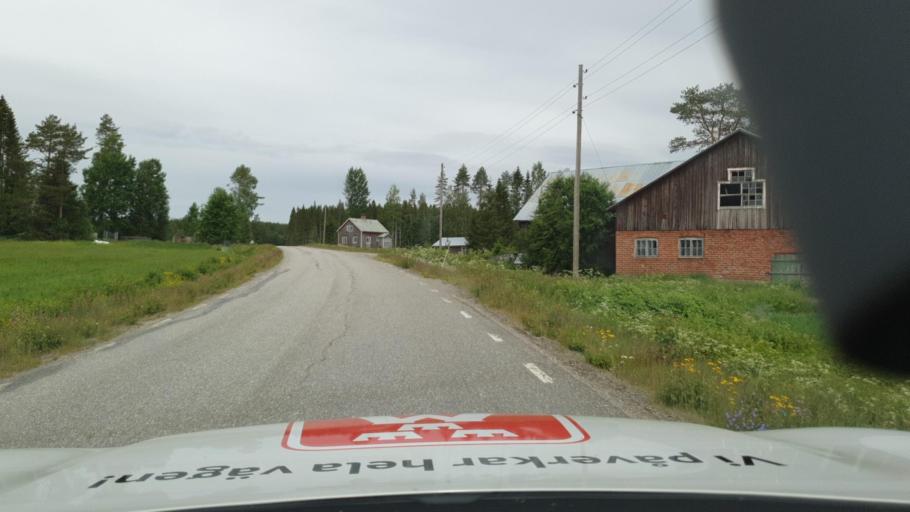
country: SE
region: Vaesterbotten
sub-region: Robertsfors Kommun
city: Robertsfors
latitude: 64.2856
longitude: 20.6541
